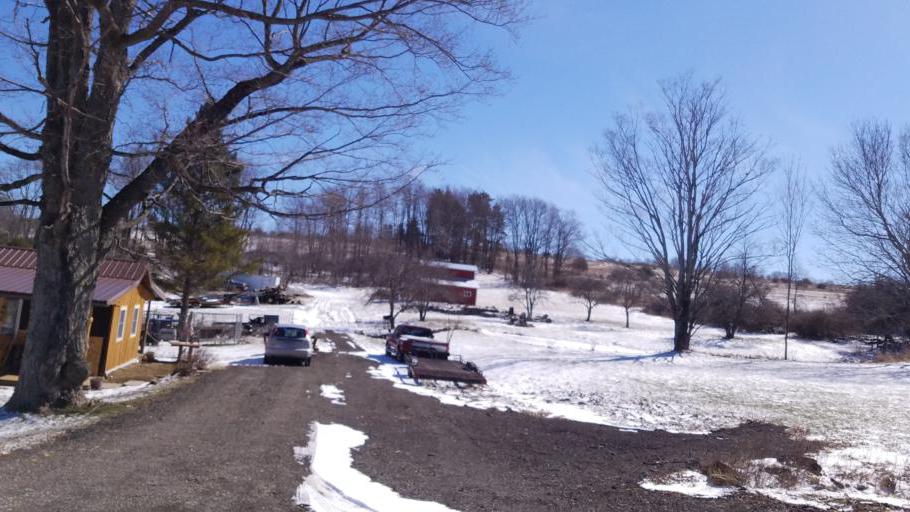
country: US
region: New York
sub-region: Allegany County
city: Andover
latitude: 42.0268
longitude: -77.7597
